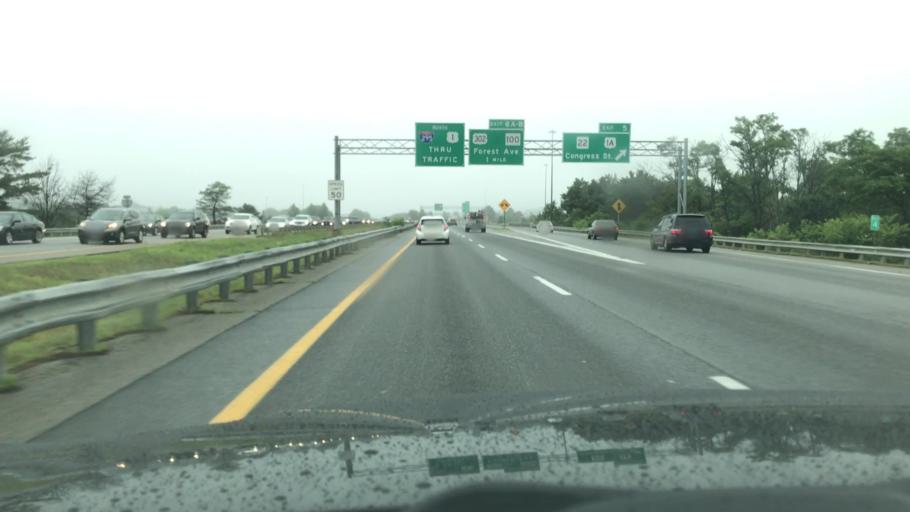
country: US
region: Maine
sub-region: Cumberland County
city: South Portland Gardens
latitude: 43.6500
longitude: -70.2889
